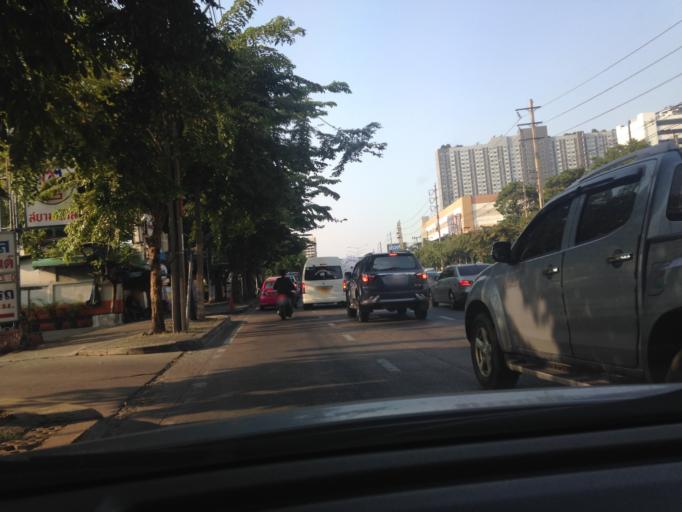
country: TH
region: Bangkok
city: Bangkok Yai
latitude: 13.7108
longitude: 100.4792
